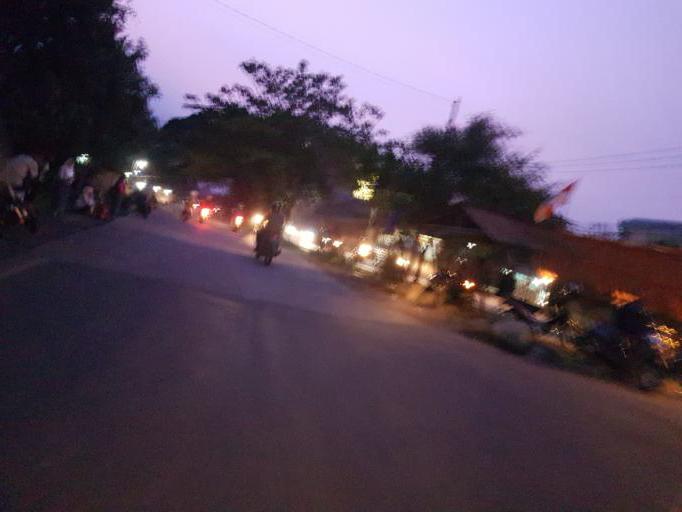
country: ID
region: West Java
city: Serpong
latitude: -6.3126
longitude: 106.6603
